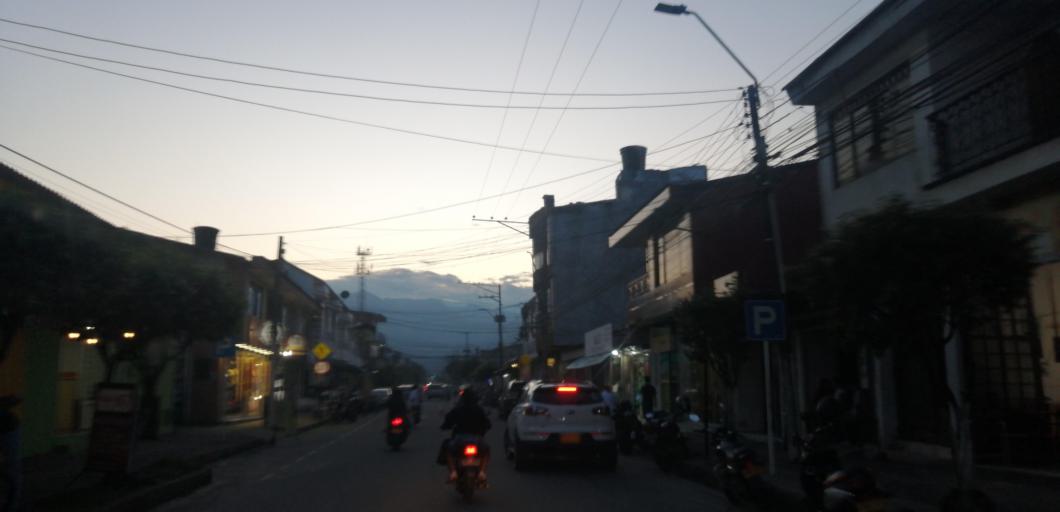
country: CO
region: Meta
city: Acacias
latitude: 3.9874
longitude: -73.7672
